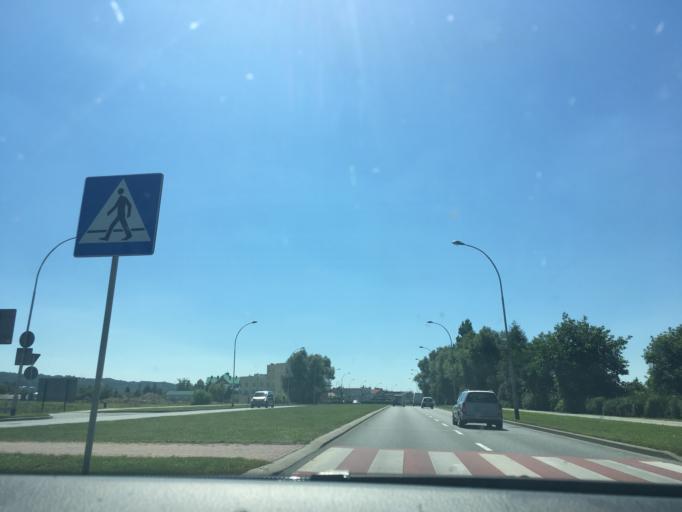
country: PL
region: Subcarpathian Voivodeship
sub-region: Rzeszow
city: Rzeszow
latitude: 50.0220
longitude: 22.0286
